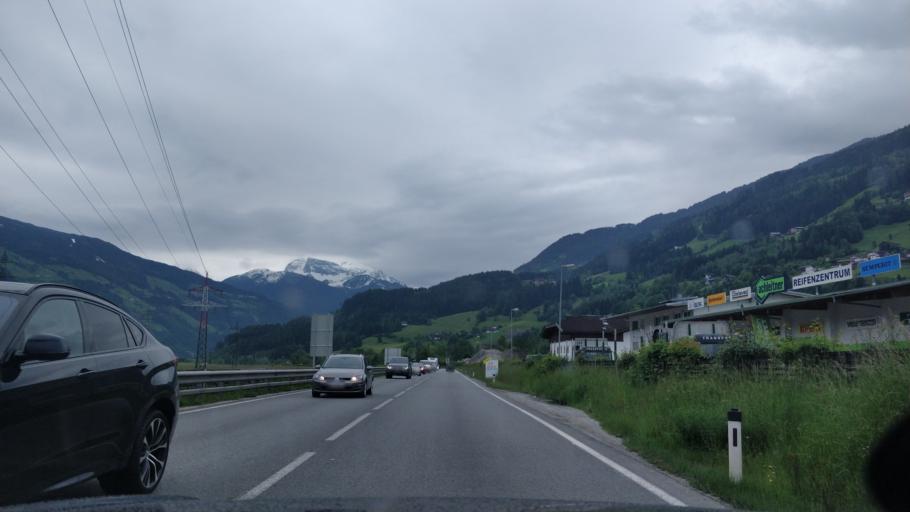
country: AT
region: Tyrol
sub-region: Politischer Bezirk Schwaz
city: Stumm
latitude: 47.2894
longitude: 11.8803
